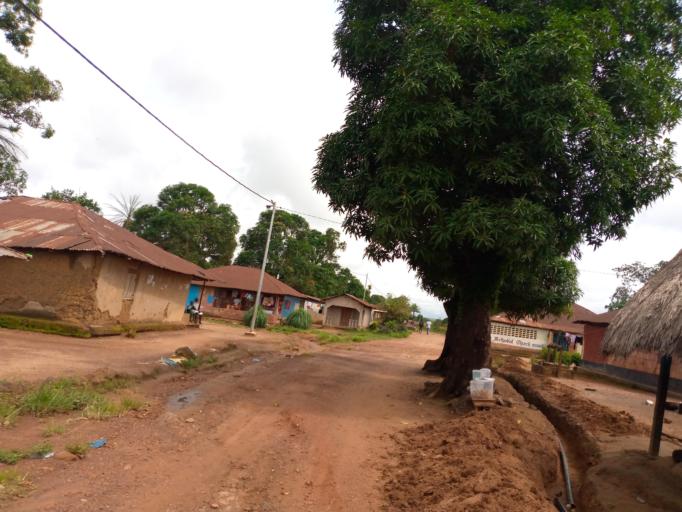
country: SL
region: Southern Province
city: Mogbwemo
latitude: 7.7633
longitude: -12.3096
